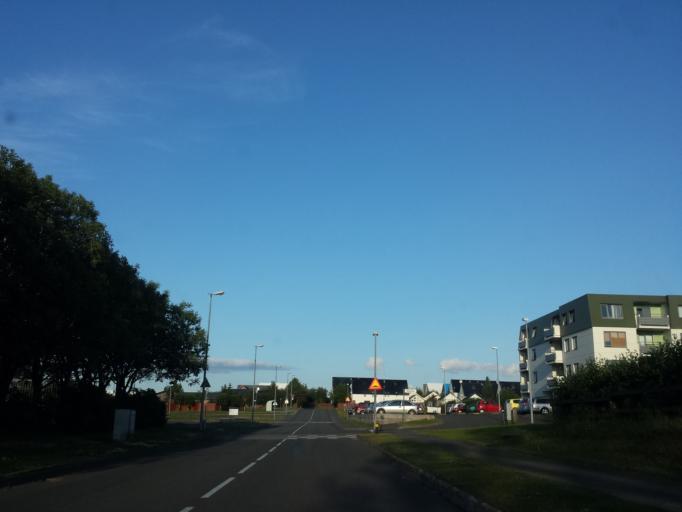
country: IS
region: Capital Region
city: Mosfellsbaer
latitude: 64.1053
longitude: -21.7860
